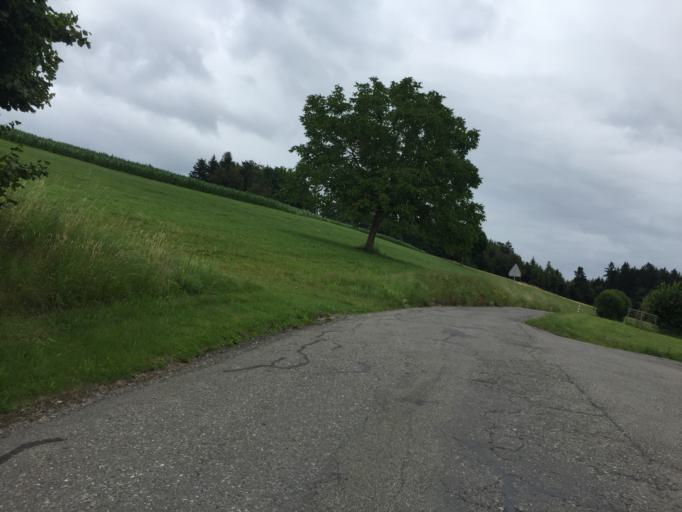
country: CH
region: Bern
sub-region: Bern-Mittelland District
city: Stettlen
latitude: 46.9501
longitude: 7.5201
